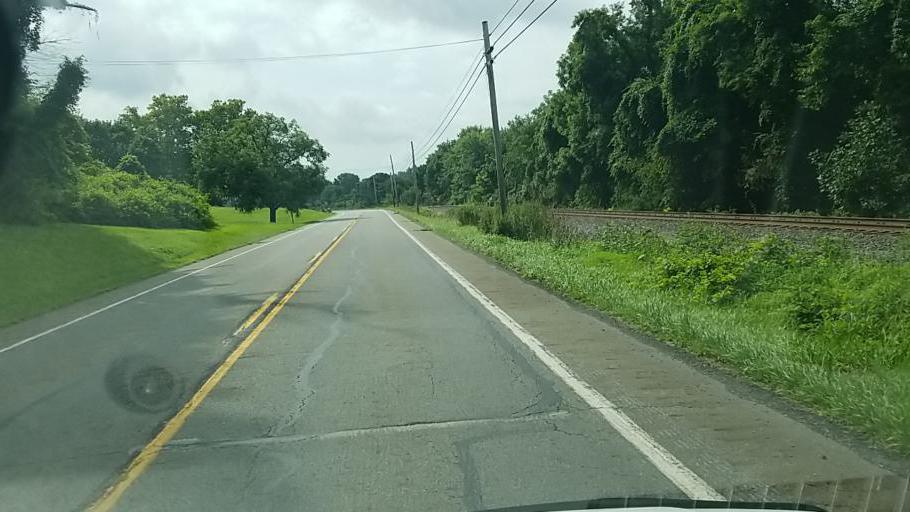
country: US
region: Pennsylvania
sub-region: Dauphin County
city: Millersburg
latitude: 40.5126
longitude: -76.9670
